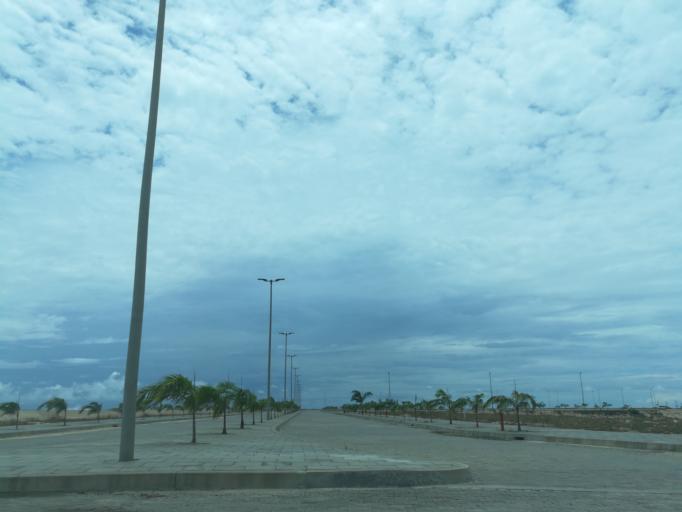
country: NG
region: Lagos
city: Ikoyi
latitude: 6.4098
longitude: 3.4199
